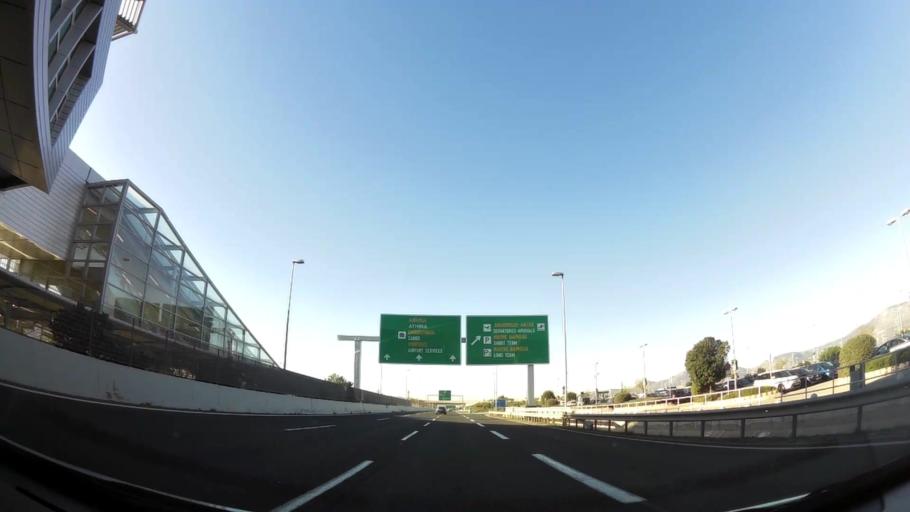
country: GR
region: Attica
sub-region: Nomarchia Anatolikis Attikis
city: Spata
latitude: 37.9367
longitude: 23.9442
